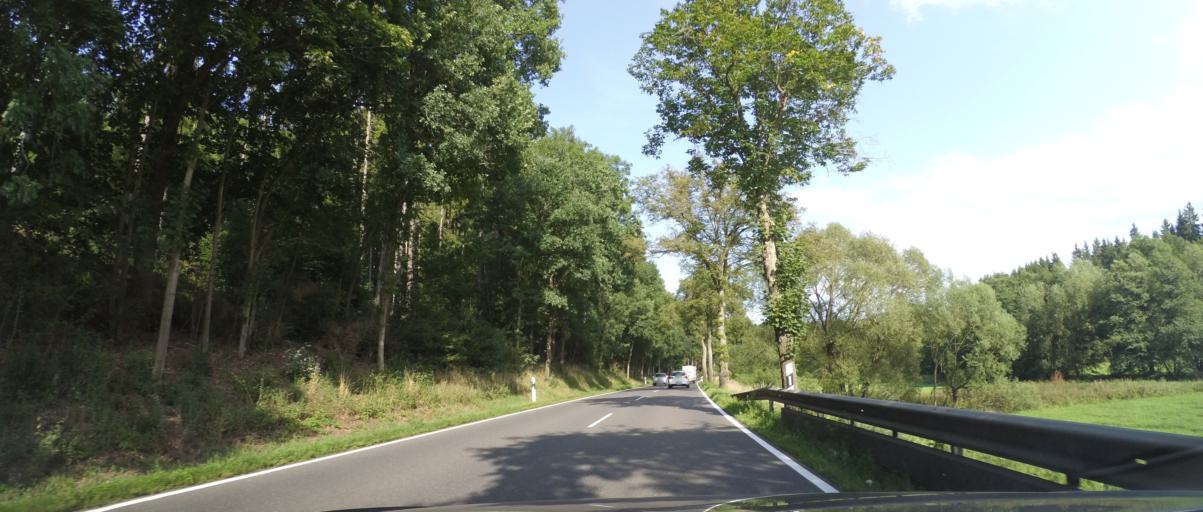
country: DE
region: Rheinland-Pfalz
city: Uxheim
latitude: 50.3851
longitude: 6.7571
